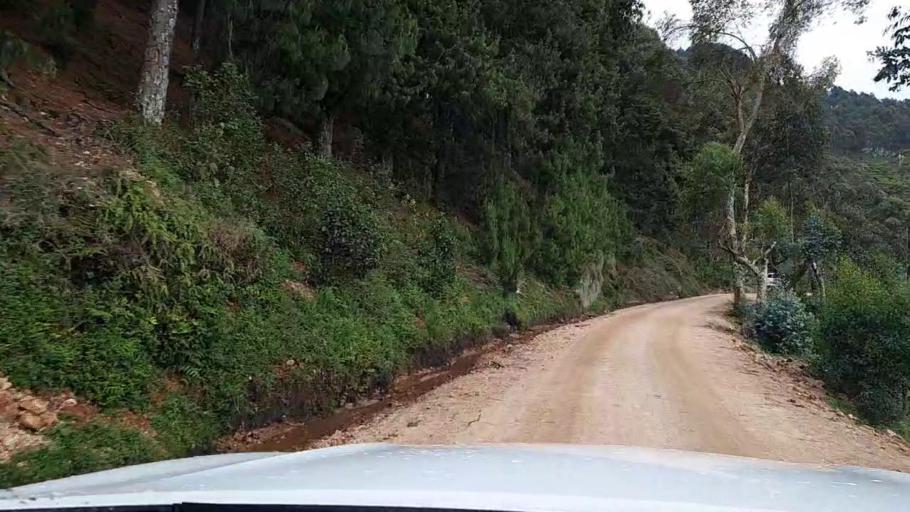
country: RW
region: Western Province
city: Kibuye
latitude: -2.2999
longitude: 29.3825
